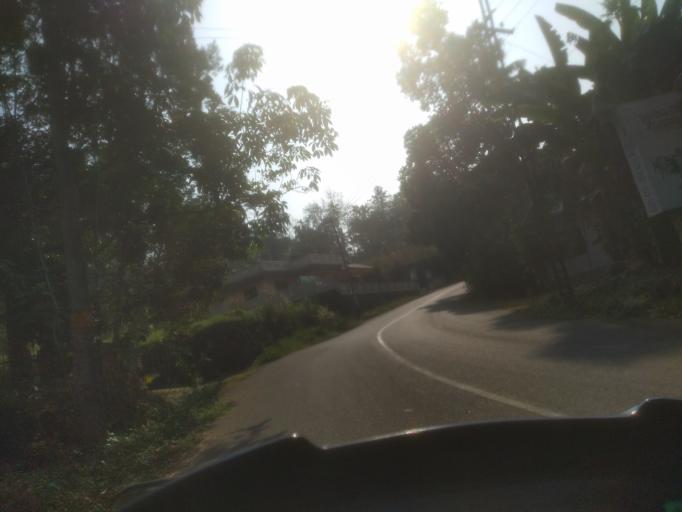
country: IN
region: Kerala
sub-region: Ernakulam
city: Piravam
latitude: 9.8694
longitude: 76.5429
